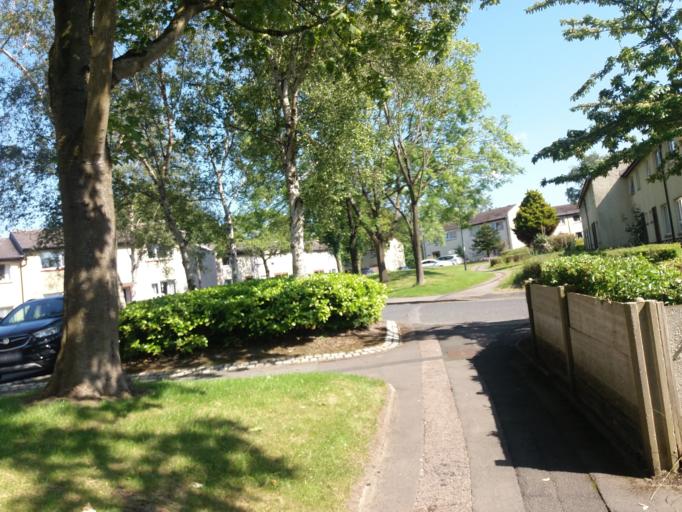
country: GB
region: England
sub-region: Lancashire
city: Clayton-le-Woods
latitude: 53.7118
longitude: -2.6379
